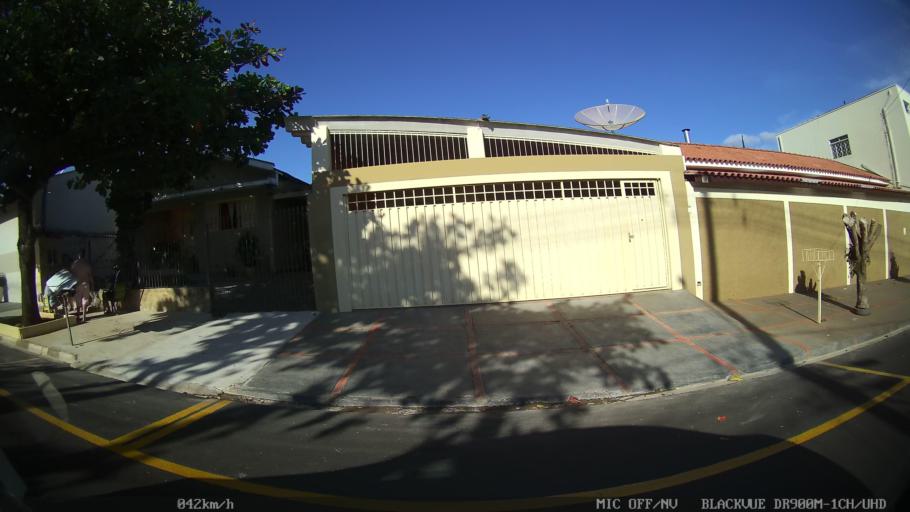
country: BR
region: Sao Paulo
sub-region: Franca
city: Franca
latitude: -20.5212
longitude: -47.4150
